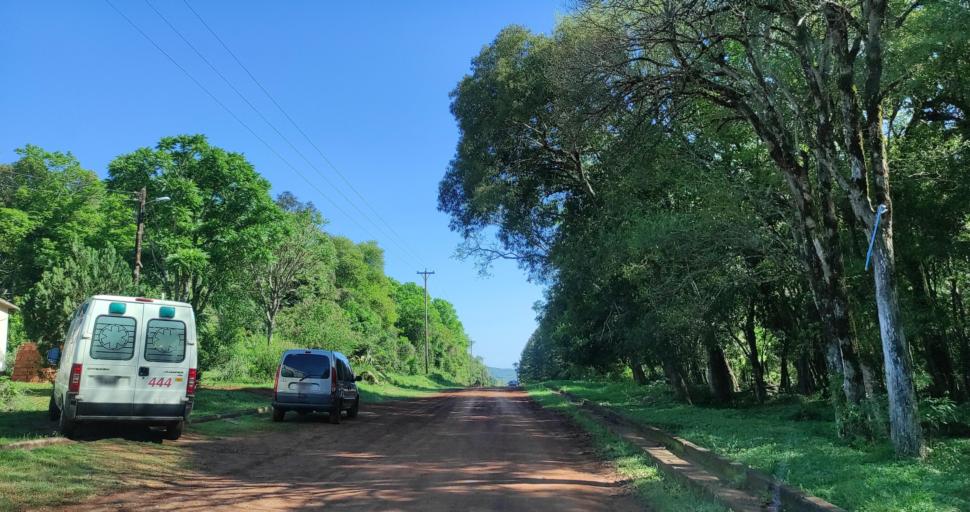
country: AR
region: Misiones
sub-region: Departamento de Candelaria
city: Loreto
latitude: -27.3299
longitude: -55.5240
